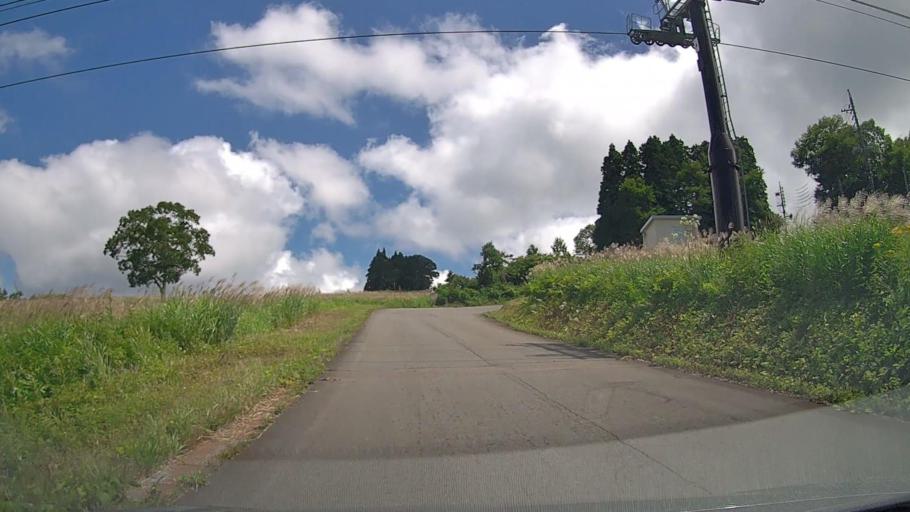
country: JP
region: Nagano
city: Iiyama
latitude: 36.9208
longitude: 138.4784
